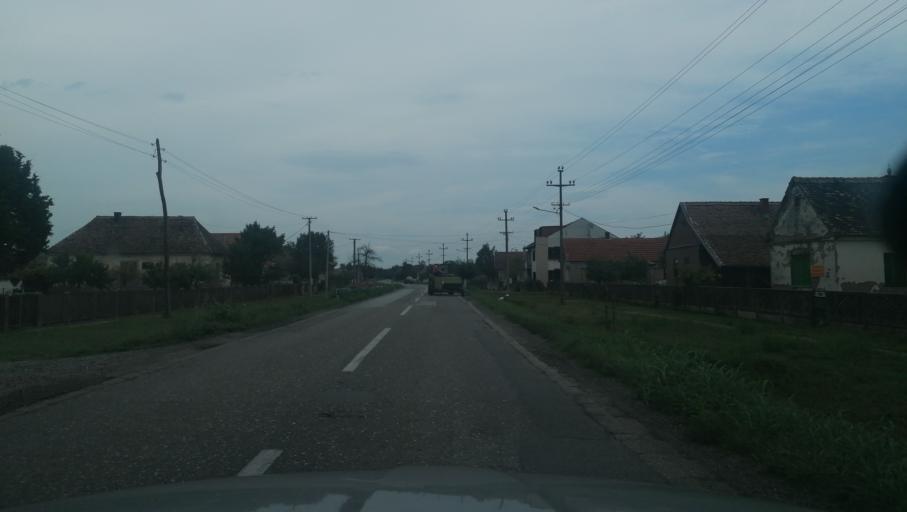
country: RS
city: Metkovic
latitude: 44.8569
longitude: 19.5463
